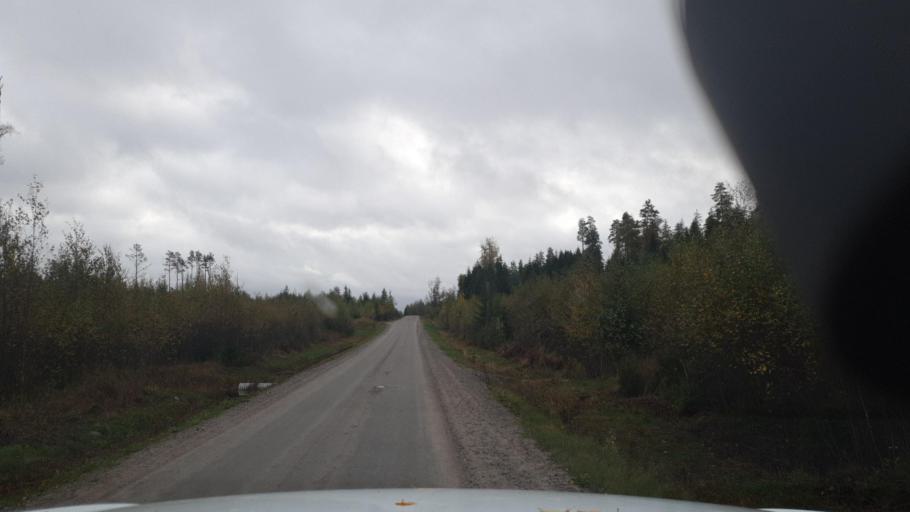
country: SE
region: Vaermland
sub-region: Karlstads Kommun
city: Edsvalla
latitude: 59.5223
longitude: 13.0038
